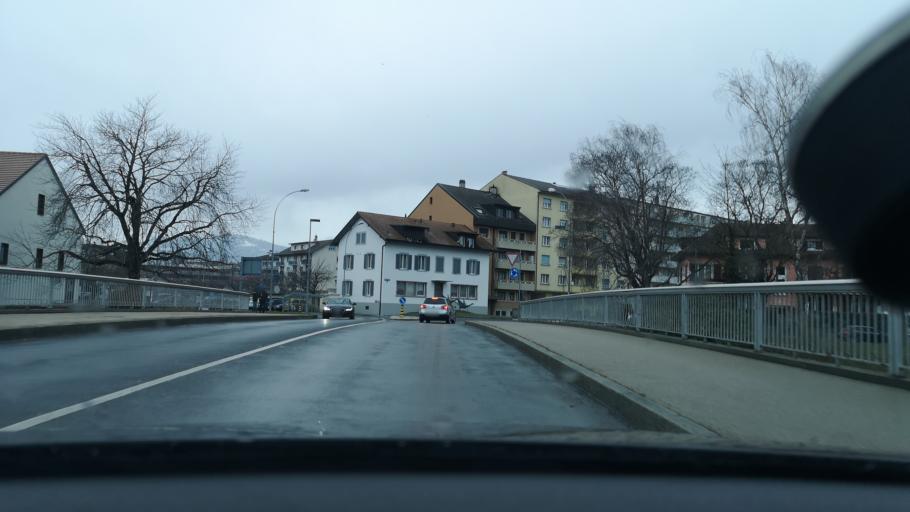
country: CH
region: Vaud
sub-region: Jura-Nord vaudois District
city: Yverdon-les-Bains
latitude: 46.7850
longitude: 6.6372
